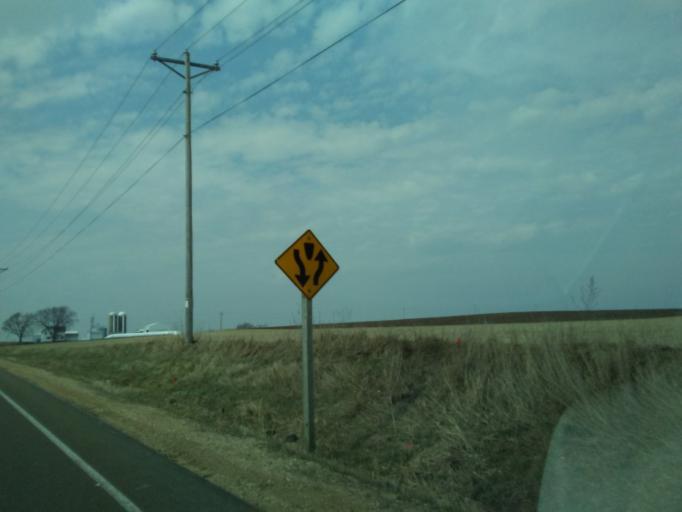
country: US
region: Wisconsin
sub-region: Dane County
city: Middleton
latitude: 43.1483
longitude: -89.4873
